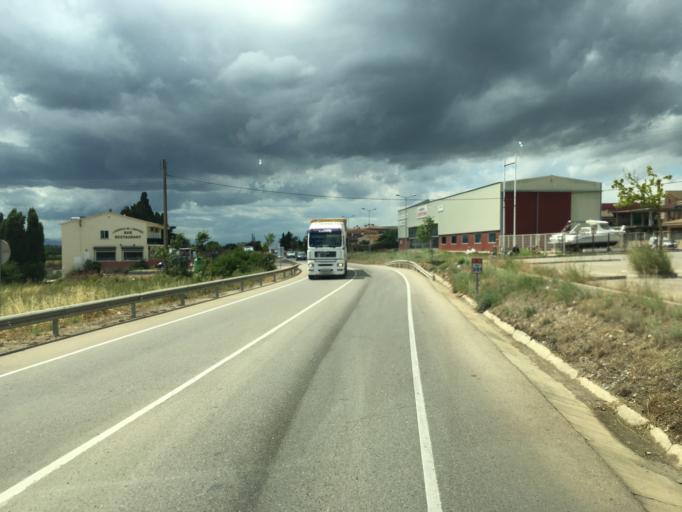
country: ES
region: Catalonia
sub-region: Provincia de Girona
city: Ulla
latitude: 42.0462
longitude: 3.1148
